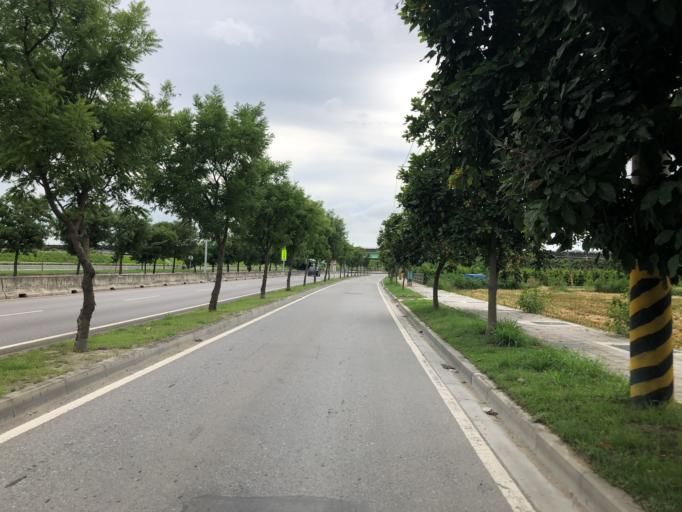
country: TW
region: Taiwan
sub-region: Taichung City
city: Taichung
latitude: 24.0833
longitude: 120.6664
